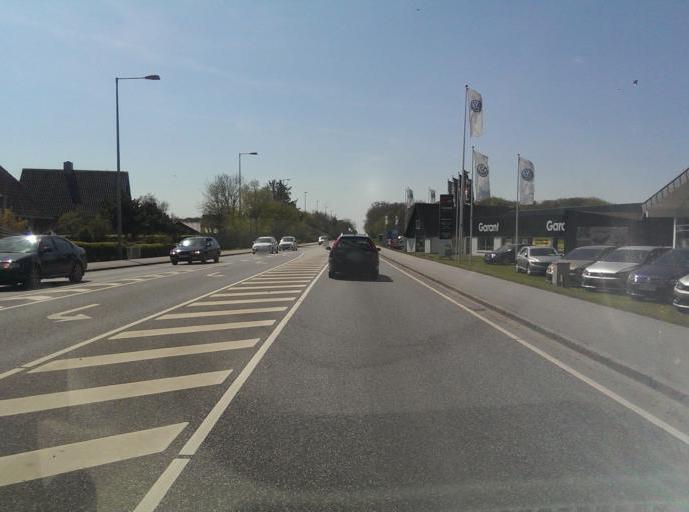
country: DK
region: South Denmark
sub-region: Esbjerg Kommune
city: Ribe
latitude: 55.3445
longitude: 8.7766
